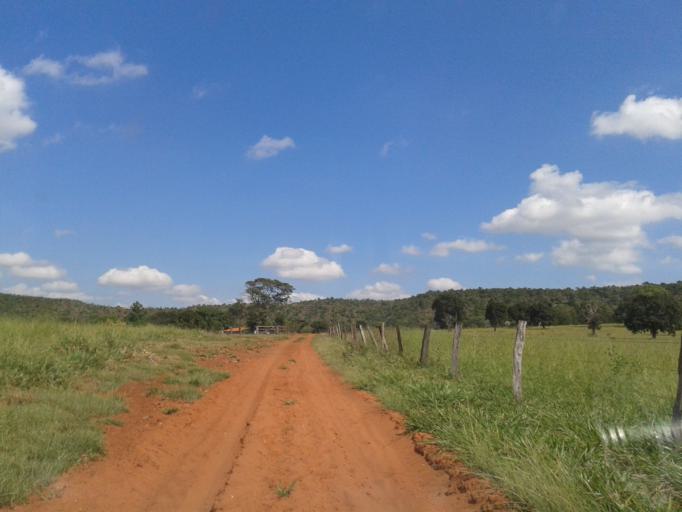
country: BR
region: Minas Gerais
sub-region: Santa Vitoria
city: Santa Vitoria
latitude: -19.2513
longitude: -50.0594
